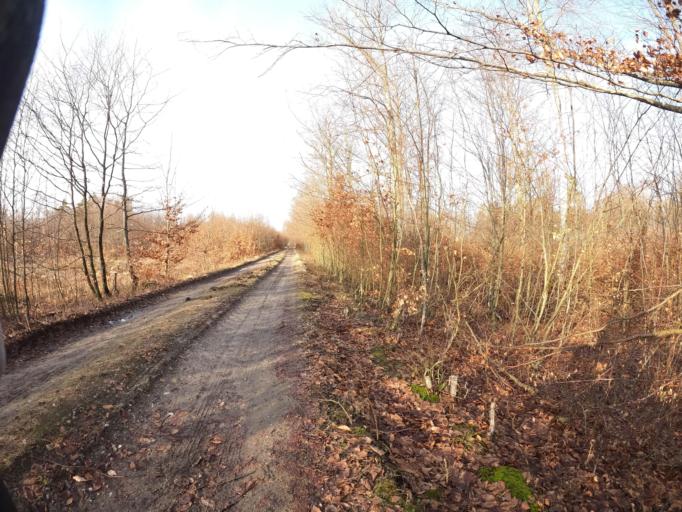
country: PL
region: West Pomeranian Voivodeship
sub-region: Powiat koszalinski
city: Polanow
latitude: 54.1547
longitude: 16.7615
